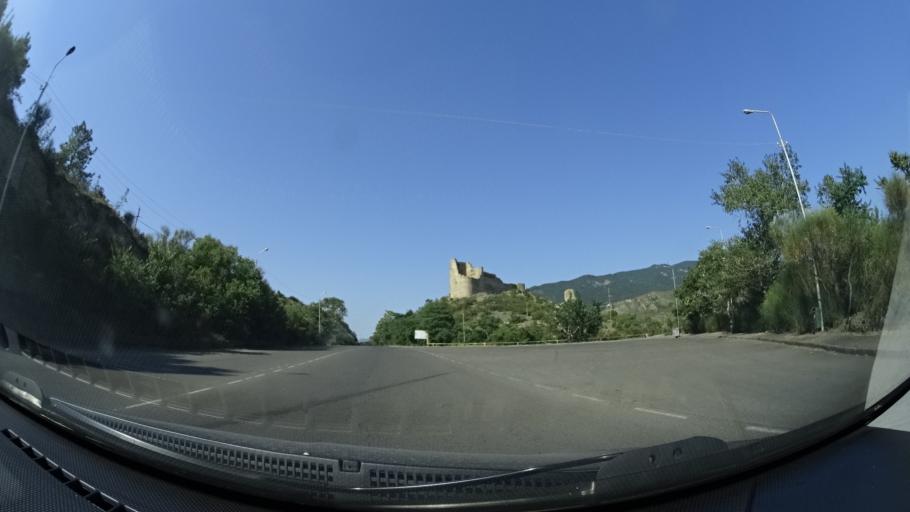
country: GE
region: Mtskheta-Mtianeti
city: Mtskheta
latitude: 41.8537
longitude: 44.7211
